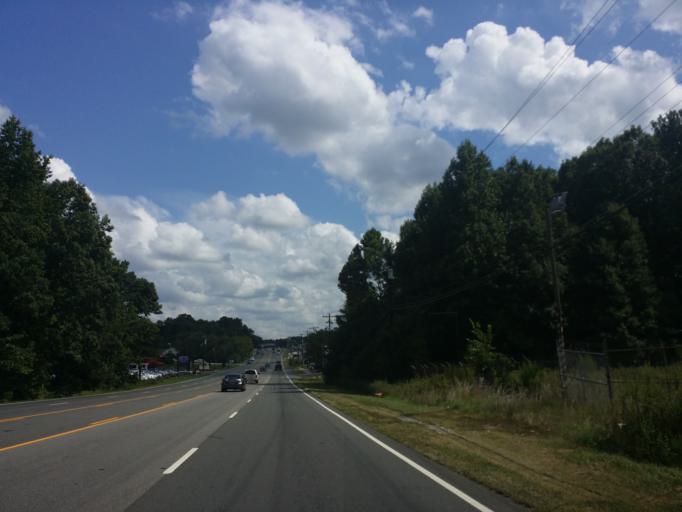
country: US
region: North Carolina
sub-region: Durham County
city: Durham
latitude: 35.9575
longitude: -78.8423
